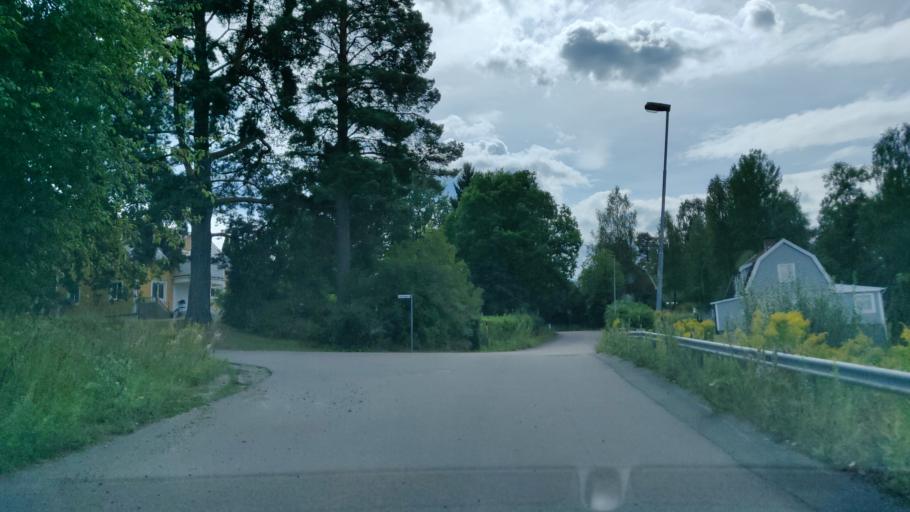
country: SE
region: Vaermland
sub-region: Hagfors Kommun
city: Hagfors
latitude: 60.0228
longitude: 13.6979
